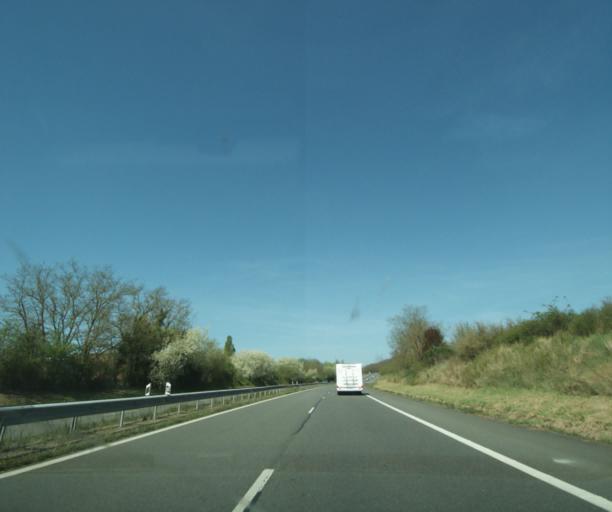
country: FR
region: Bourgogne
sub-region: Departement de la Nievre
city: Chaulgnes
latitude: 47.1046
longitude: 3.0720
